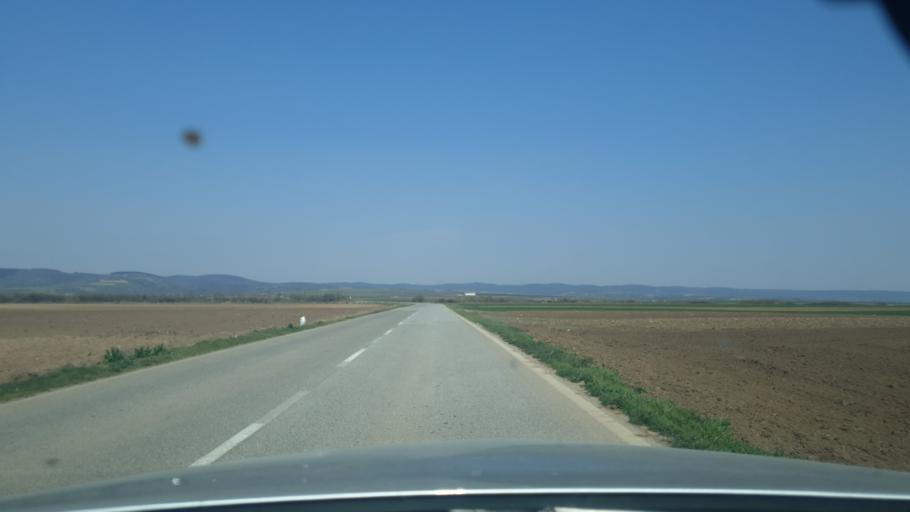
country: RS
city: Vrdnik
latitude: 45.0656
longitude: 19.7692
